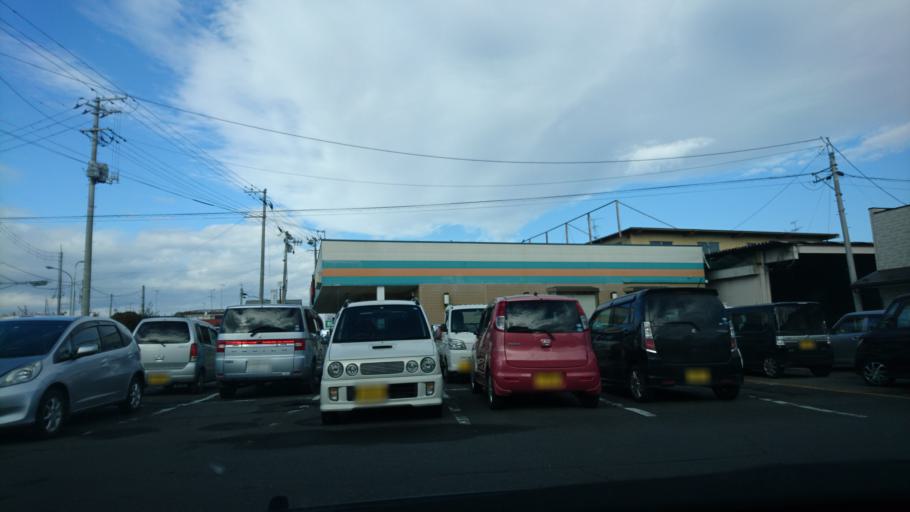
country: JP
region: Miyagi
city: Wakuya
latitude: 38.6810
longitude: 141.1953
